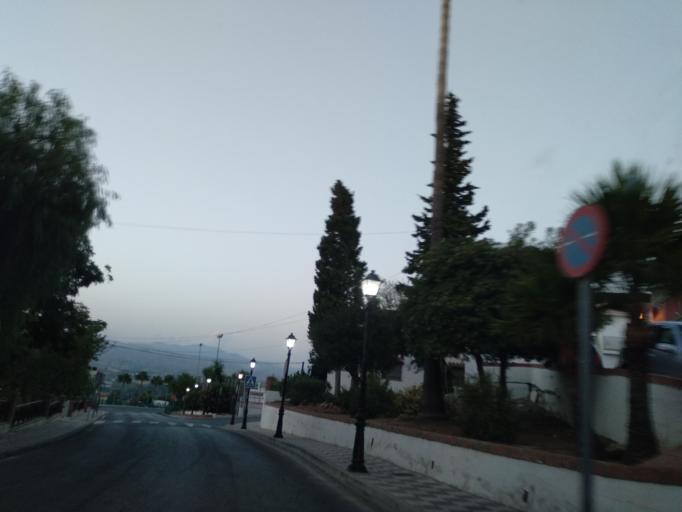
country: ES
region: Andalusia
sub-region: Provincia de Malaga
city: Cartama
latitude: 36.7128
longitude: -4.6276
